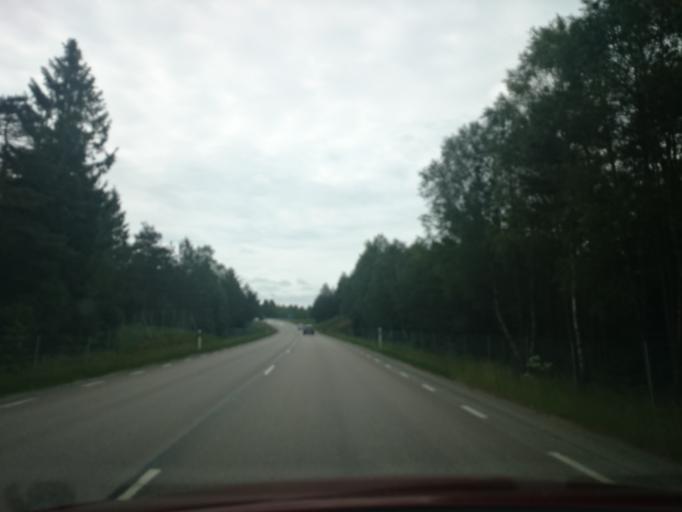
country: SE
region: Vaestra Goetaland
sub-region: Harryda Kommun
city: Hindas
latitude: 57.6785
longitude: 12.3559
